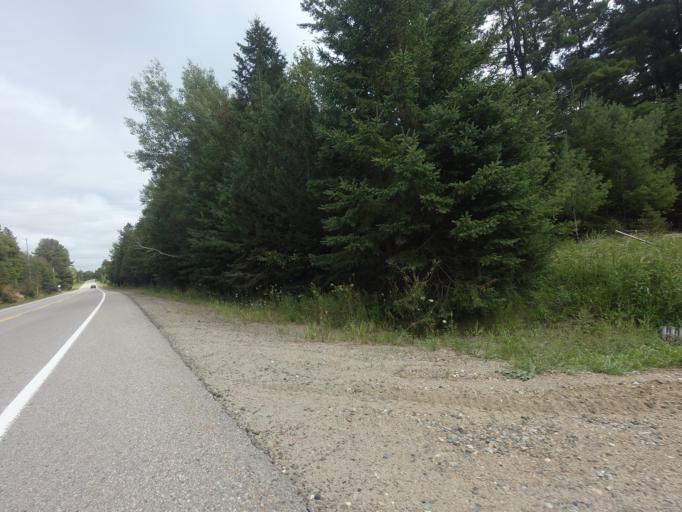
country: CA
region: Ontario
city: Bancroft
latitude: 44.9066
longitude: -78.4101
